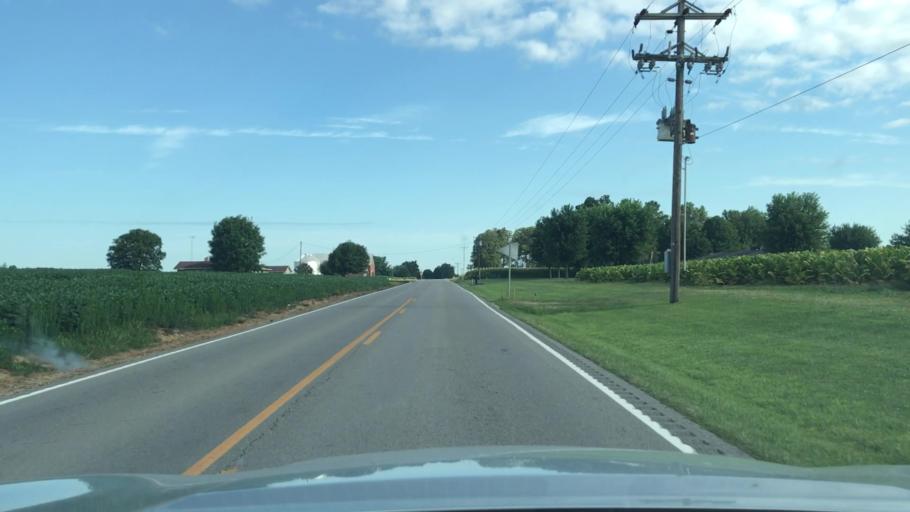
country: US
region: Kentucky
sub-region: Todd County
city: Elkton
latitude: 36.8690
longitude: -87.1638
